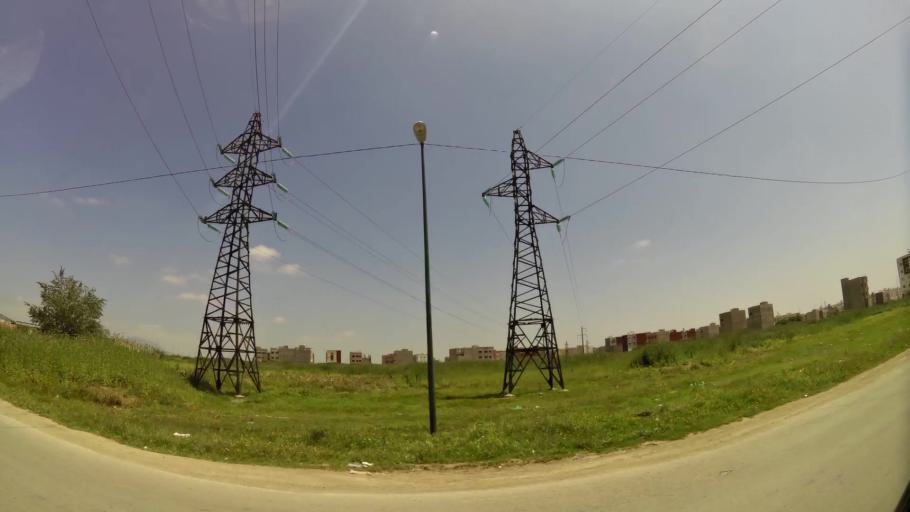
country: MA
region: Fes-Boulemane
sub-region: Fes
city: Fes
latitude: 34.0365
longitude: -5.0604
